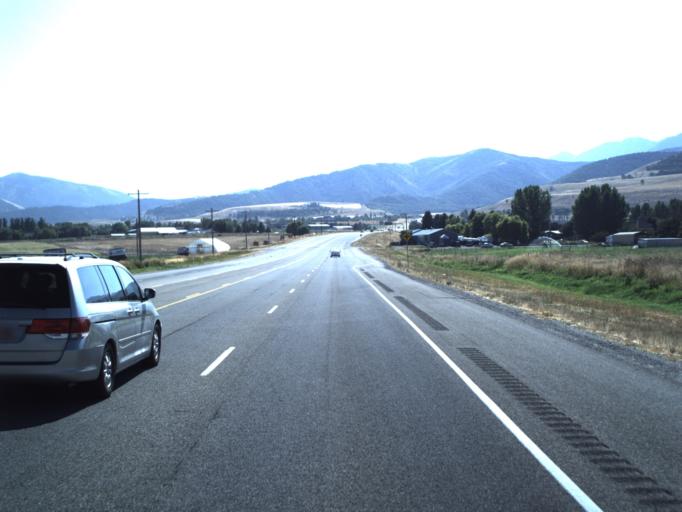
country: US
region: Utah
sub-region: Cache County
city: Wellsville
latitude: 41.6256
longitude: -111.9265
